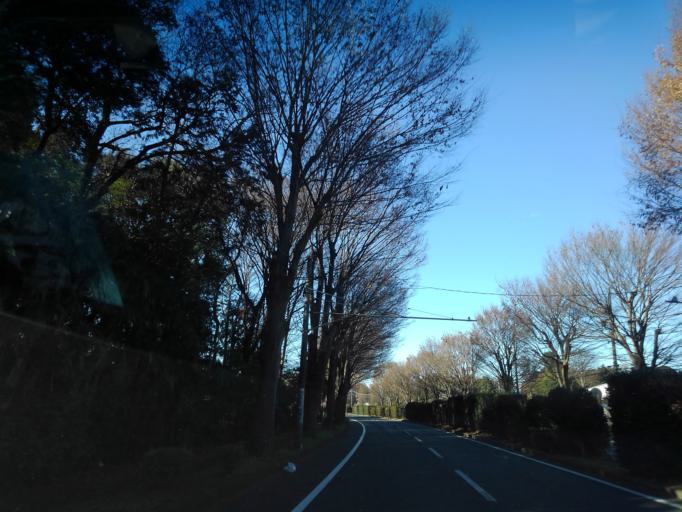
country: JP
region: Saitama
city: Oi
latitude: 35.8085
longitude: 139.5156
